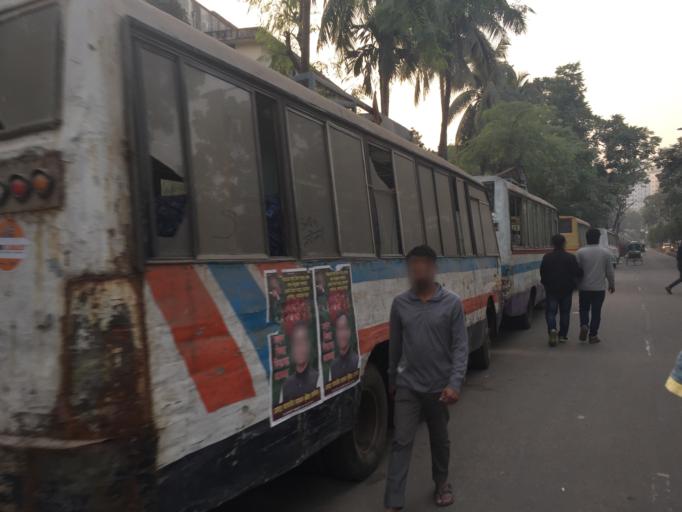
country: BD
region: Dhaka
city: Paltan
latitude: 23.7363
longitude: 90.4195
